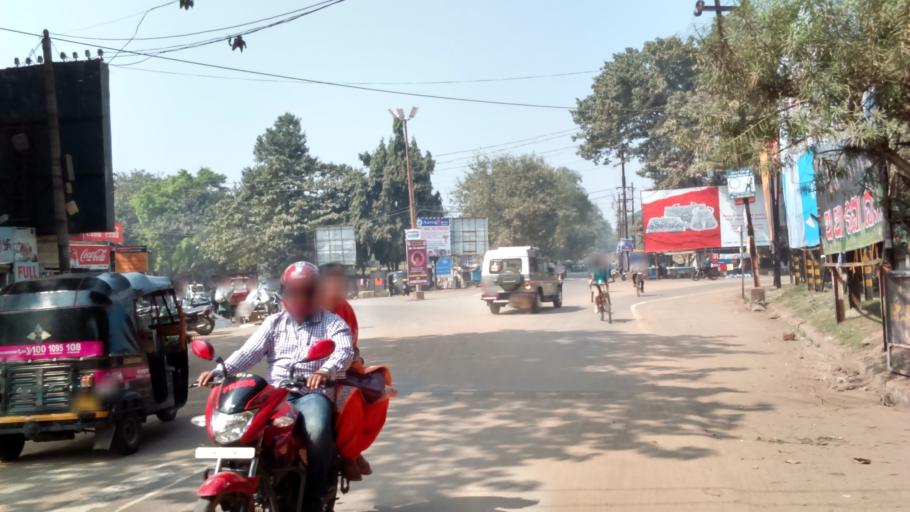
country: IN
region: Odisha
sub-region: Cuttack
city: Cuttack
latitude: 20.4829
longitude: 85.8705
